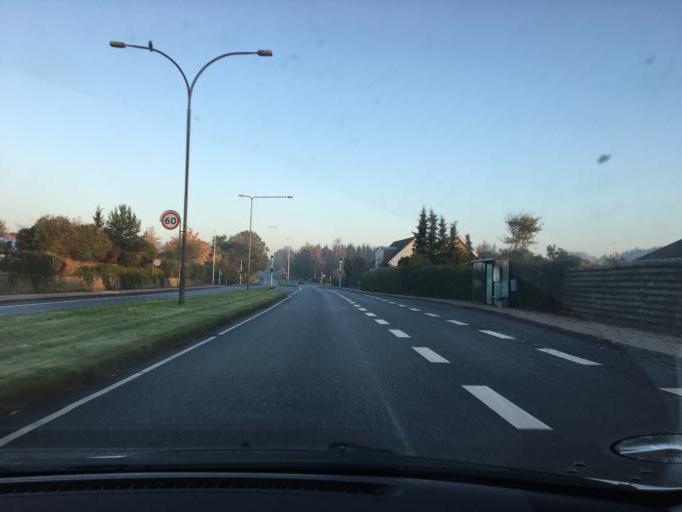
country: DK
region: South Denmark
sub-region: Vejle Kommune
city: Vejle
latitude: 55.6849
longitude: 9.5269
